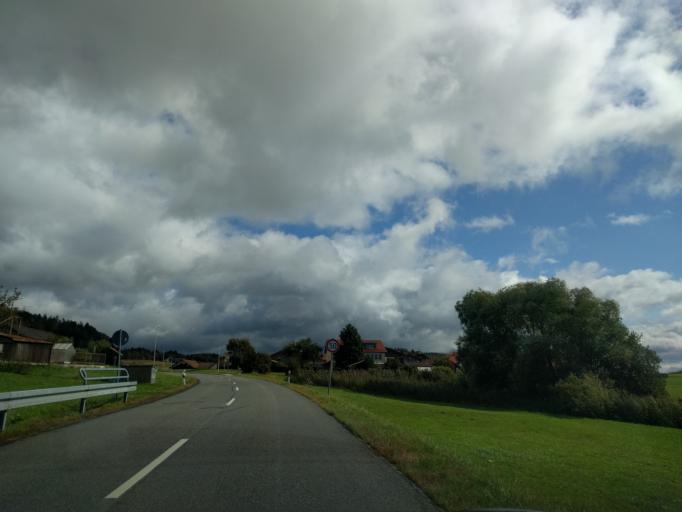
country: DE
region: Bavaria
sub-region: Lower Bavaria
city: Deggendorf
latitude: 48.8335
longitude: 13.0004
